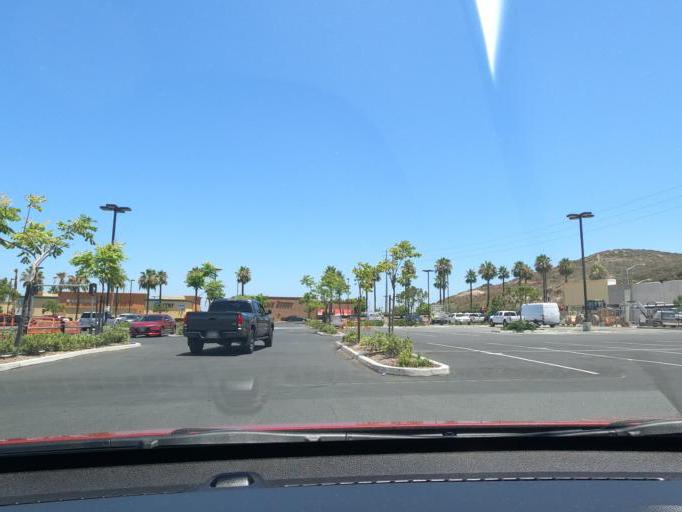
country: US
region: California
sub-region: San Diego County
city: Imperial Beach
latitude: 32.5761
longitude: -117.0361
